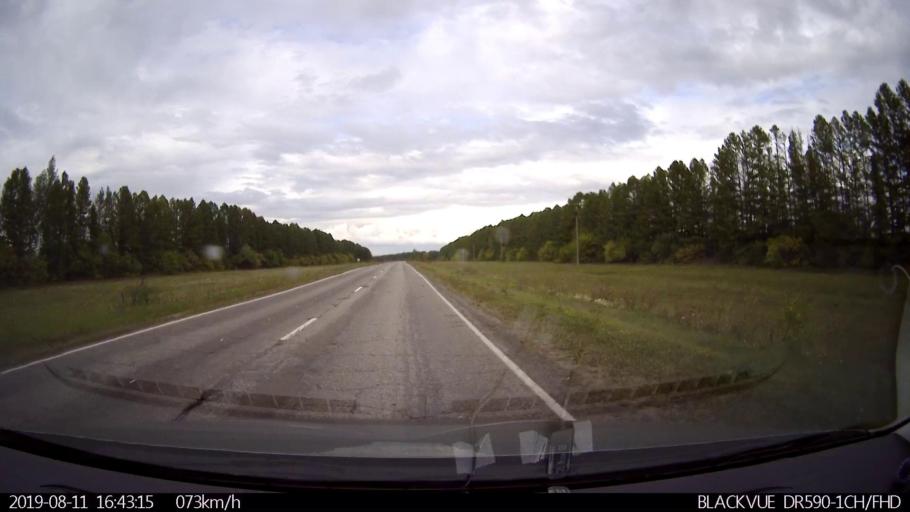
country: RU
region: Ulyanovsk
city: Mayna
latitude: 54.1672
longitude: 47.6700
